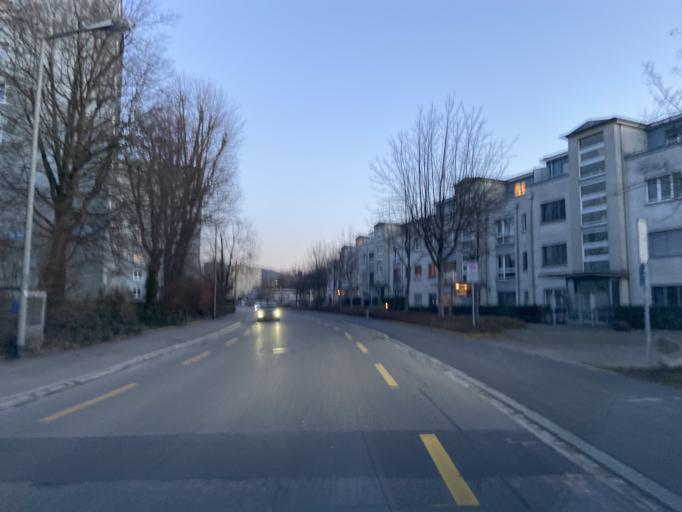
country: CH
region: Zurich
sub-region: Bezirk Winterthur
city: Wuelflingen (Kreis 6) / Haerti
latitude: 47.5136
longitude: 8.6832
